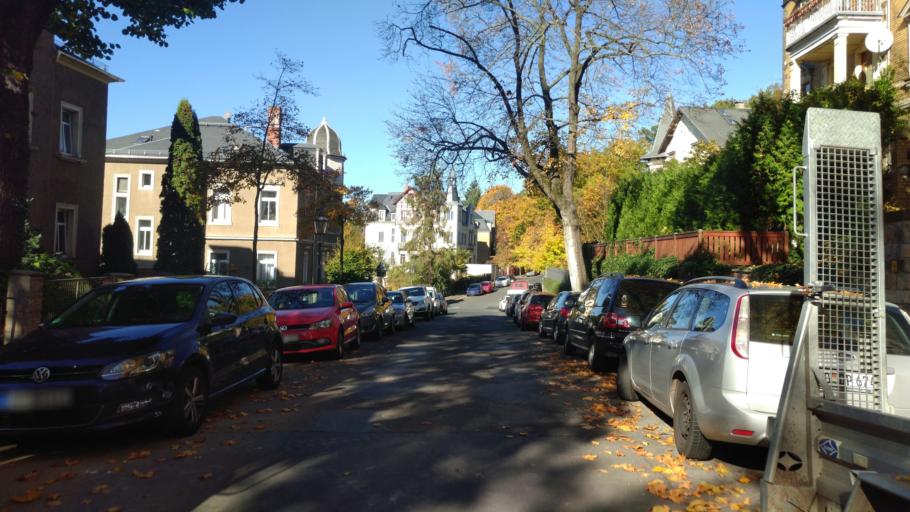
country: DE
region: Saxony
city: Albertstadt
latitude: 51.0941
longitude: 13.7311
